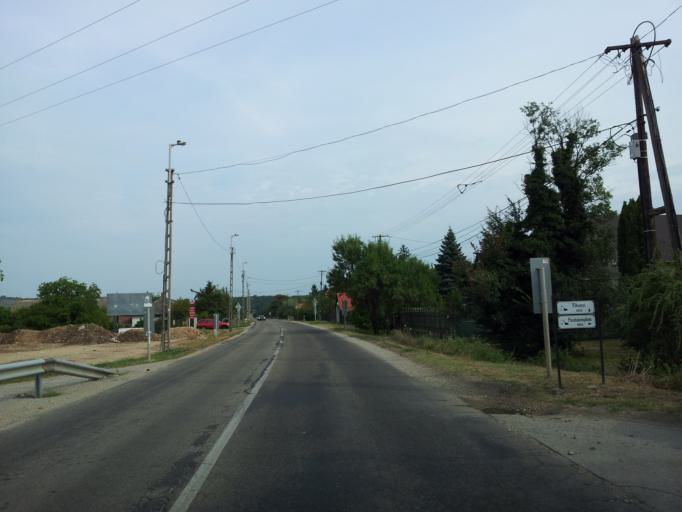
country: HU
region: Veszprem
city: Balatonfured
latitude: 46.9264
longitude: 17.8374
